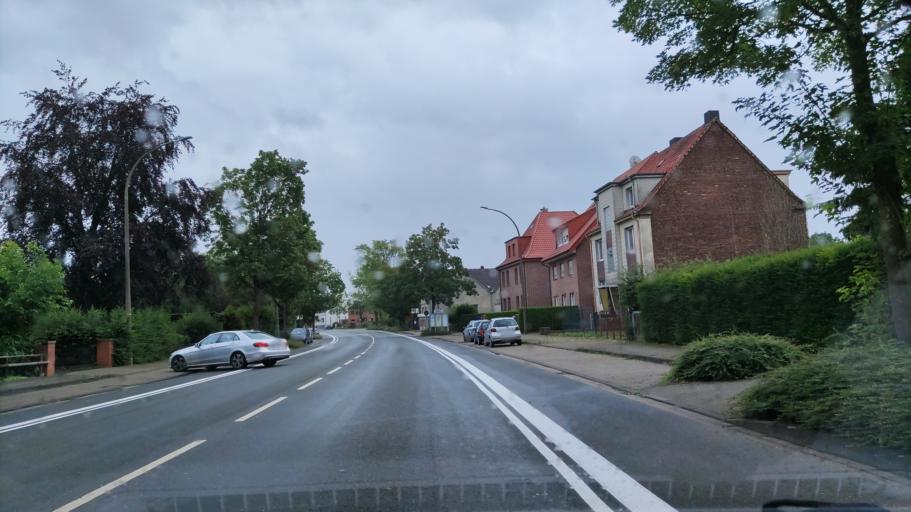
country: DE
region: North Rhine-Westphalia
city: Ahlen
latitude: 51.7703
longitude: 7.8712
